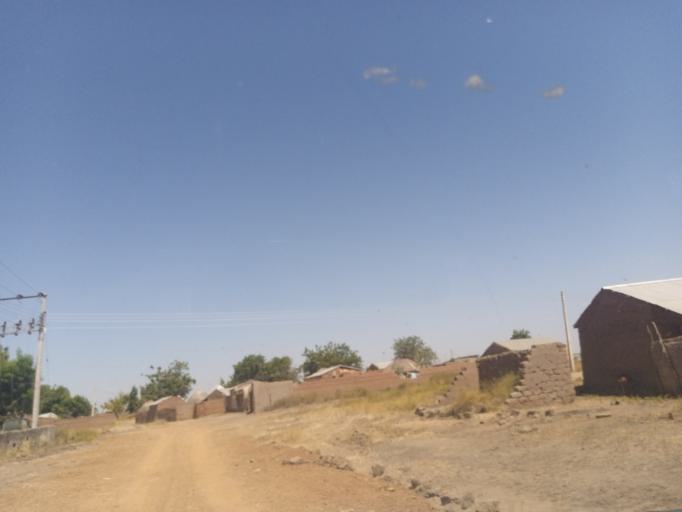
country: NG
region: Adamawa
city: Yola
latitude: 9.3107
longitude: 12.8901
